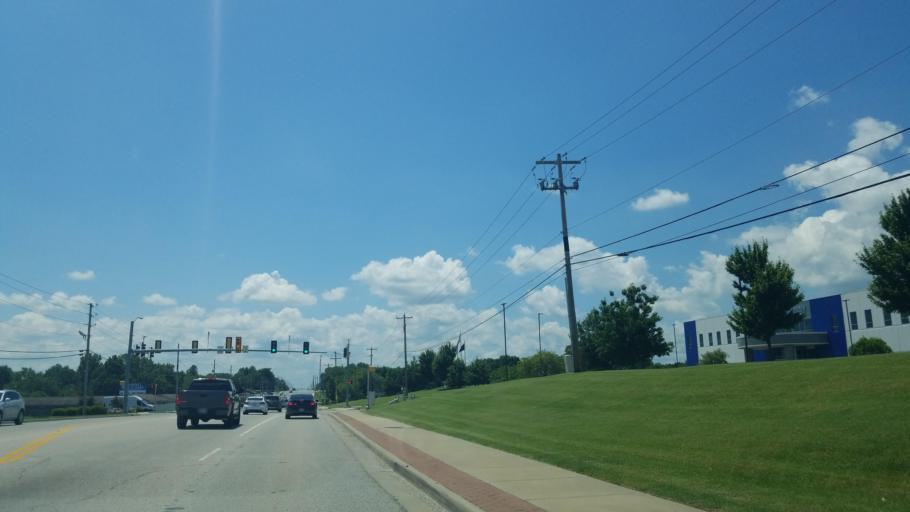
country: US
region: Oklahoma
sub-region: Tulsa County
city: Broken Arrow
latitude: 36.0592
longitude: -95.7797
